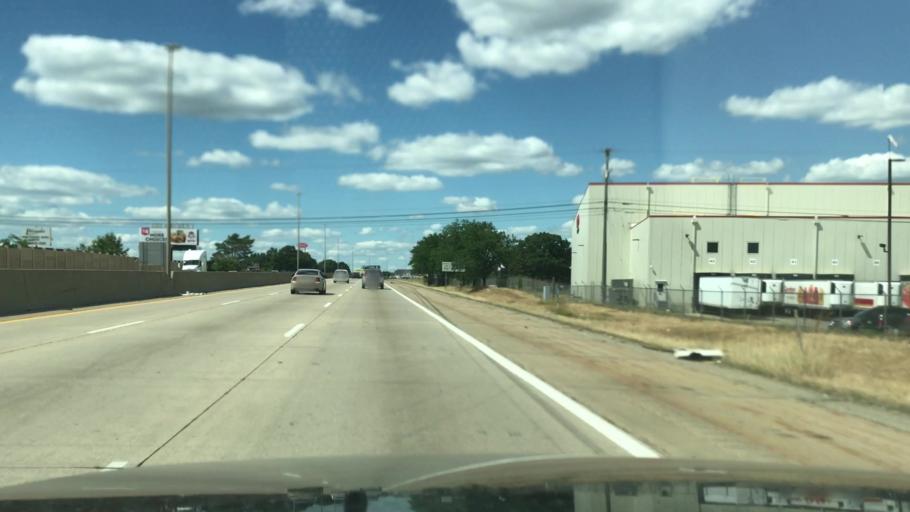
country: US
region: Michigan
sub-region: Kent County
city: Cutlerville
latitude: 42.8724
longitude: -85.6810
